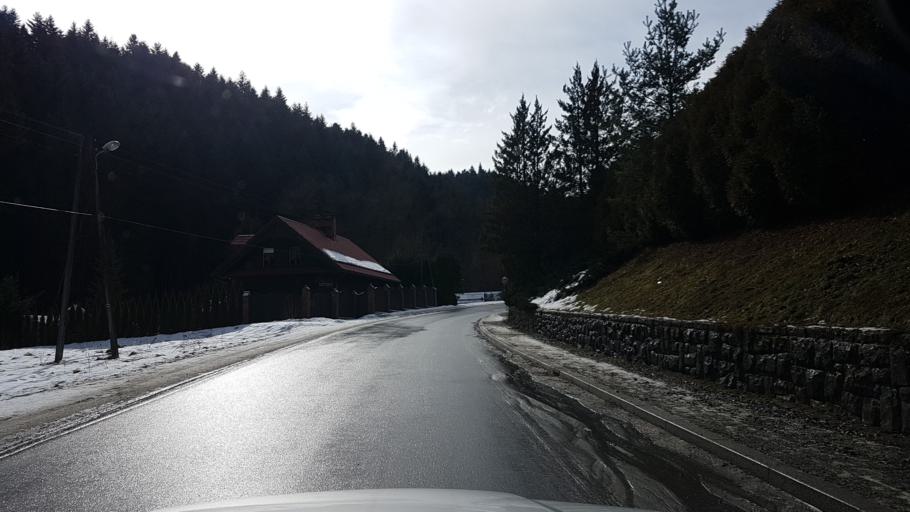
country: PL
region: Lesser Poland Voivodeship
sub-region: Powiat nowosadecki
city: Piwniczna-Zdroj
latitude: 49.4323
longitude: 20.6791
